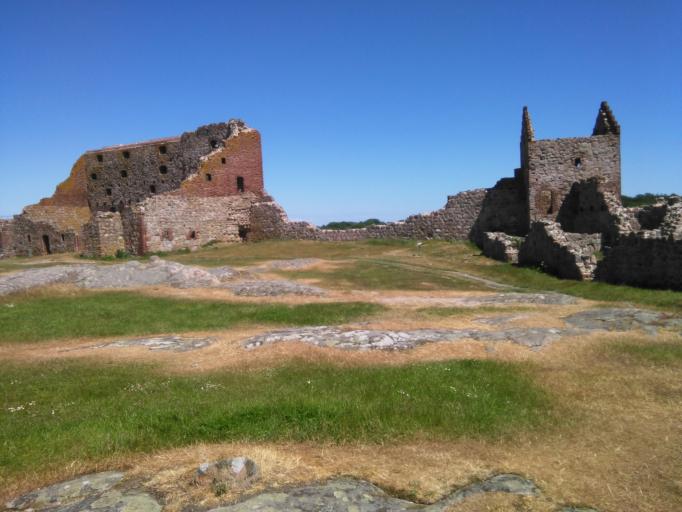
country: DK
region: Capital Region
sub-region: Bornholm Kommune
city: Ronne
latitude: 55.2709
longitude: 14.7557
